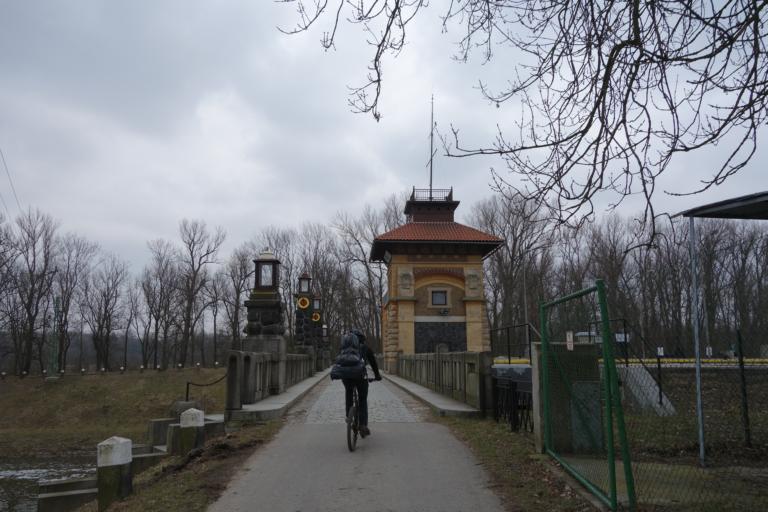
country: CZ
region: Central Bohemia
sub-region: Okres Melnik
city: Melnik
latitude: 50.3411
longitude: 14.4681
